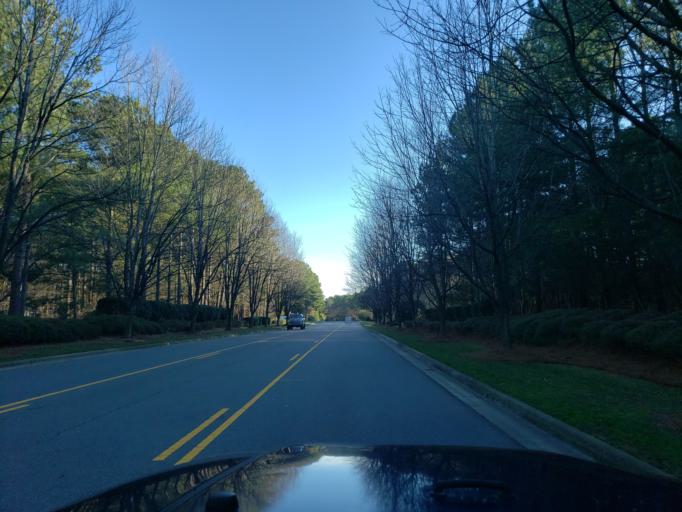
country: US
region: North Carolina
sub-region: Catawba County
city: Lake Norman of Catawba
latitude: 35.5504
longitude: -80.9231
